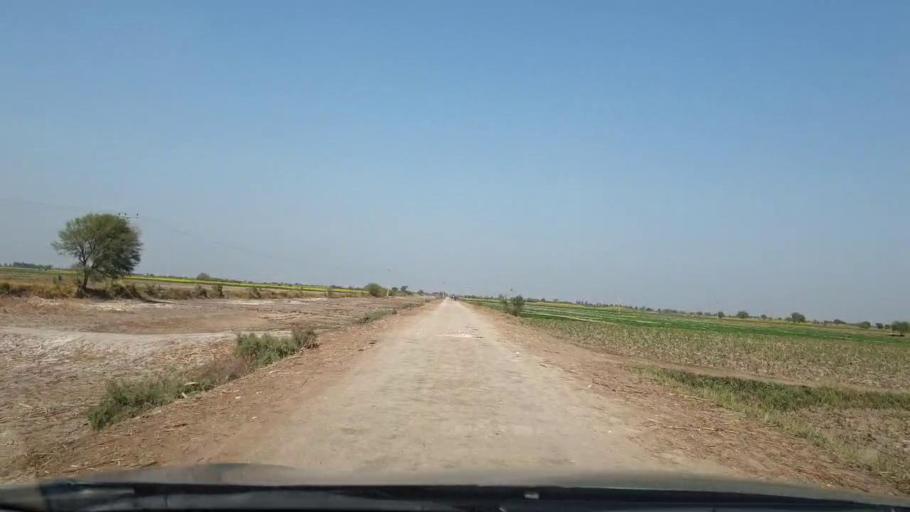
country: PK
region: Sindh
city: Mirpur Khas
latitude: 25.5957
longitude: 68.8890
